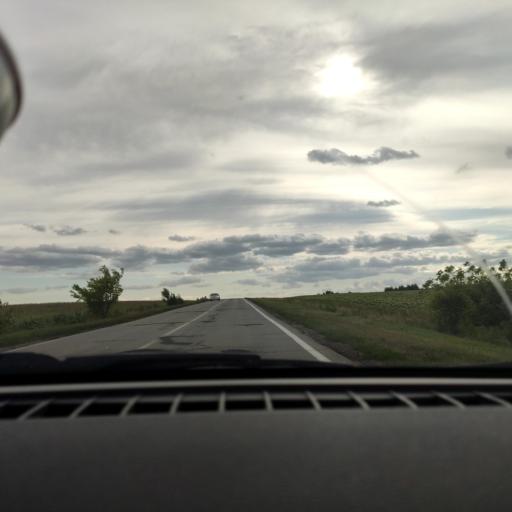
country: RU
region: Samara
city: Krasnyy Yar
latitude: 53.4336
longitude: 50.5599
